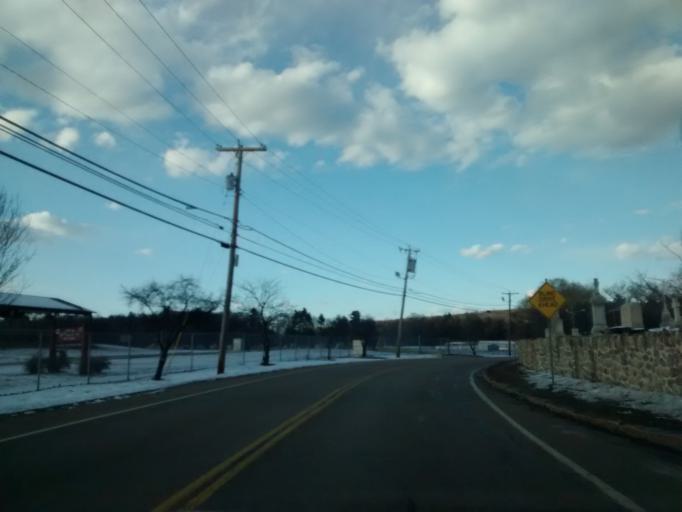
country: US
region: Massachusetts
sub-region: Worcester County
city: Milford
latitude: 42.1550
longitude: -71.5098
